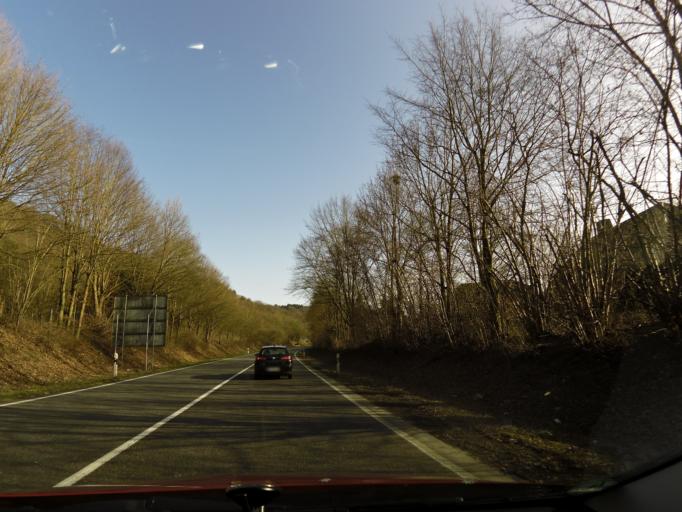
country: DE
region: Rheinland-Pfalz
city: Rheinbrohl
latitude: 50.5064
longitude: 7.3284
